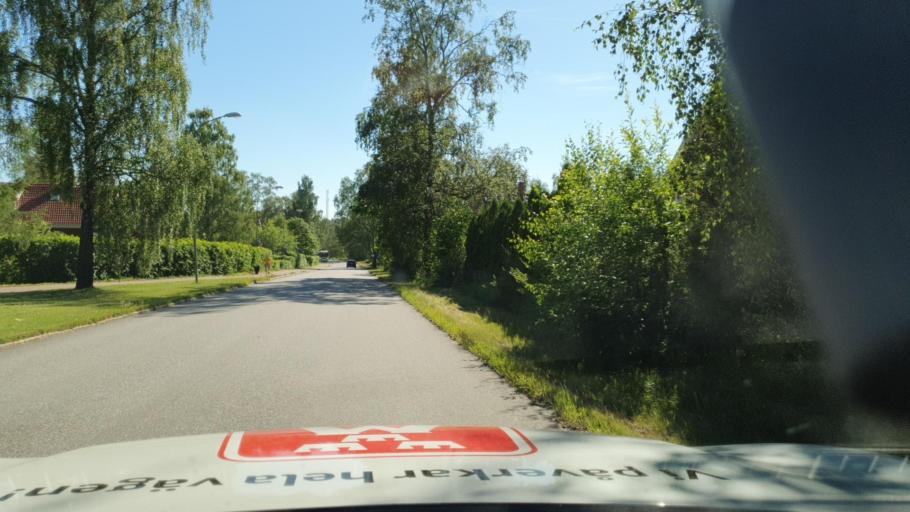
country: SE
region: OErebro
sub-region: Karlskoga Kommun
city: Karlskoga
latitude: 59.3374
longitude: 14.5532
